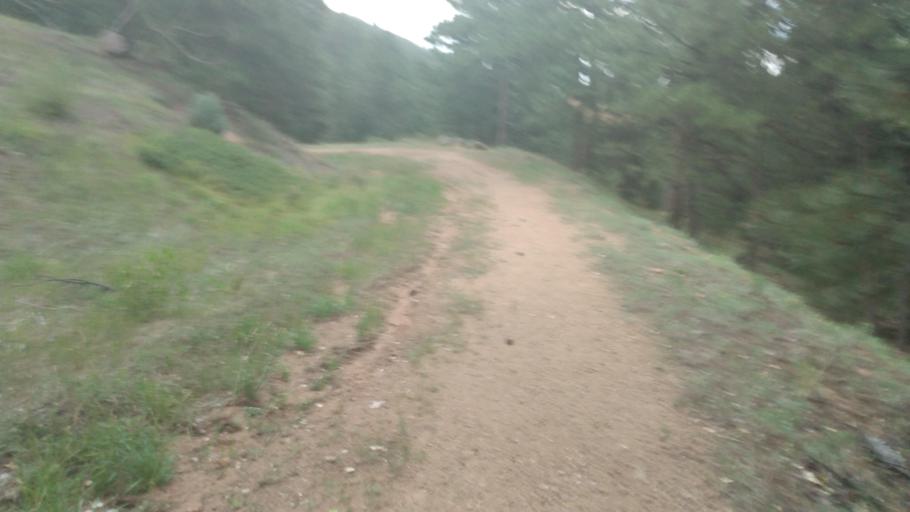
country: US
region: Colorado
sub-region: Boulder County
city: Boulder
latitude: 39.9966
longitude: -105.3088
